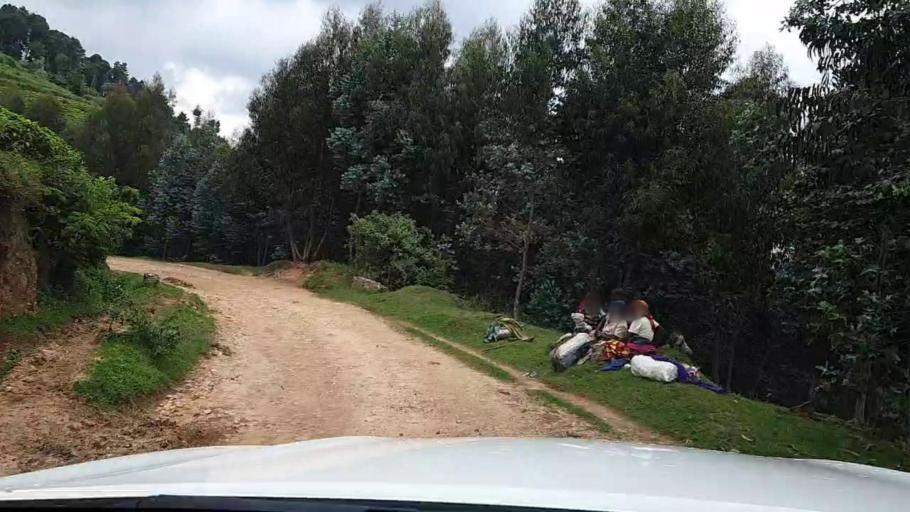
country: RW
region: Western Province
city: Kibuye
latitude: -2.2874
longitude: 29.3749
